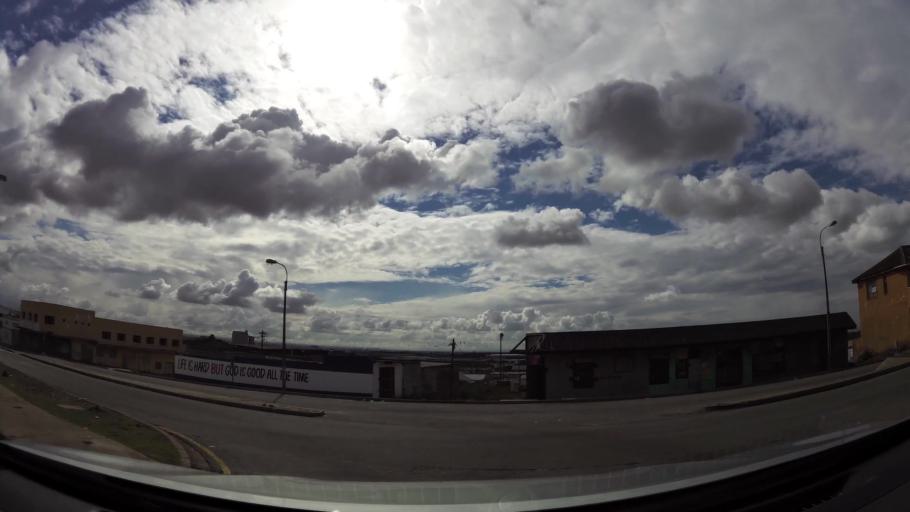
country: ZA
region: Eastern Cape
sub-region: Nelson Mandela Bay Metropolitan Municipality
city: Port Elizabeth
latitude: -33.9332
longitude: 25.5758
